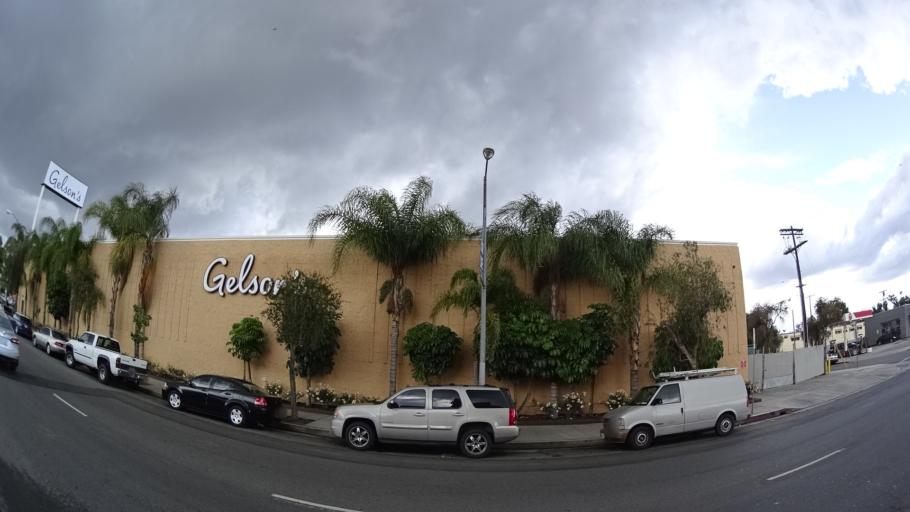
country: US
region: California
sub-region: Los Angeles County
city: North Hollywood
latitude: 34.1562
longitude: -118.3965
